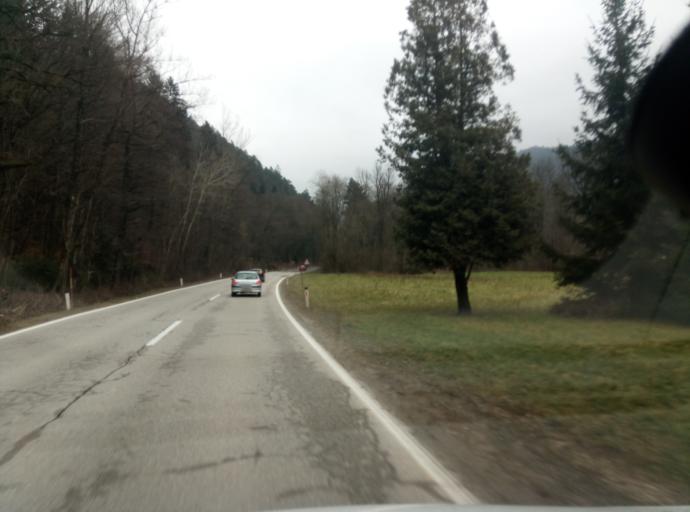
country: SI
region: Moravce
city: Moravce
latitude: 46.0951
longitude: 14.6920
